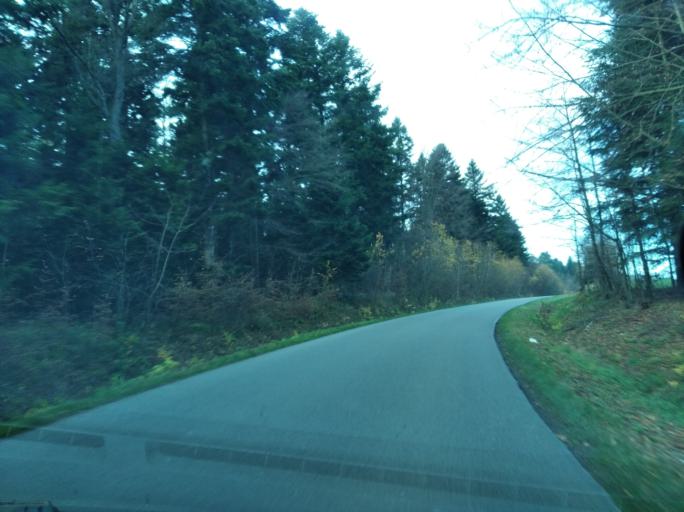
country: PL
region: Subcarpathian Voivodeship
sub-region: Powiat ropczycko-sedziszowski
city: Zagorzyce
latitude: 49.9546
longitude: 21.6950
